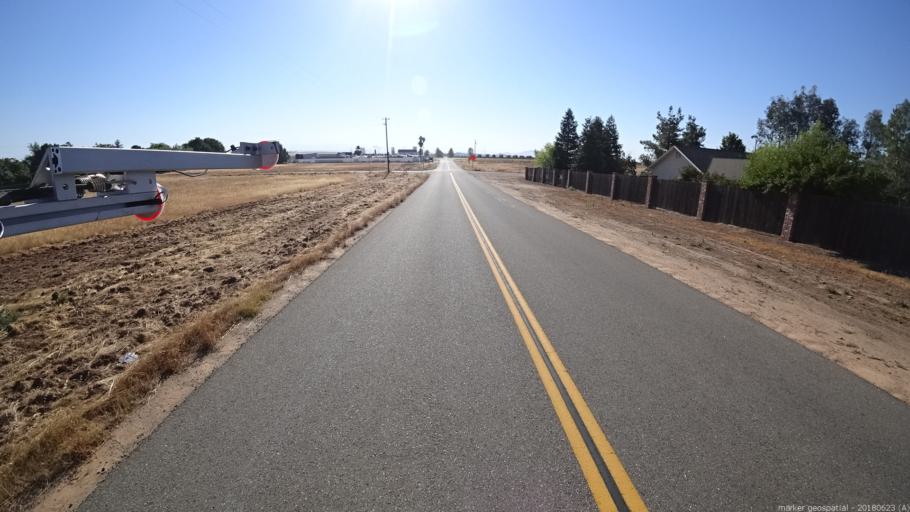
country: US
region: California
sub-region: Madera County
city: Bonadelle Ranchos-Madera Ranchos
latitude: 36.9595
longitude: -119.7970
